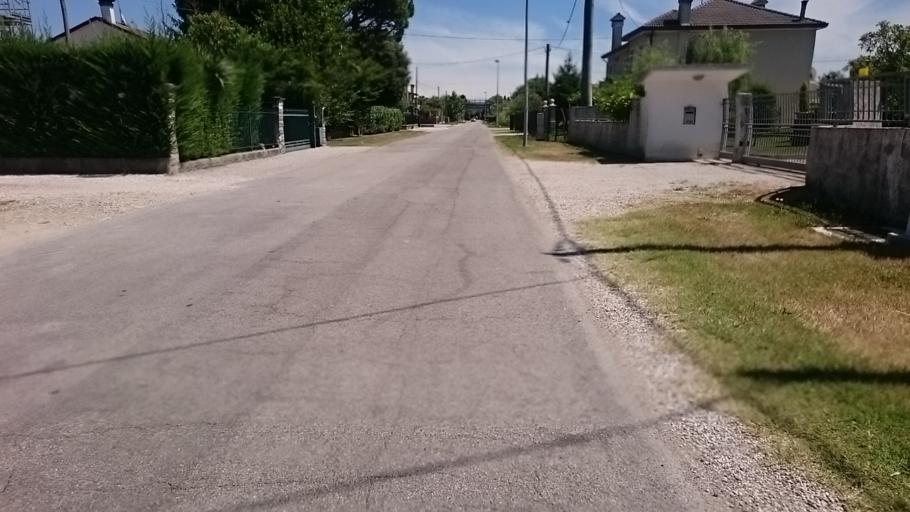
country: IT
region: Veneto
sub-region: Provincia di Padova
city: Borgoricco-San Michele delle Badesse-Sant'Eufemia
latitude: 45.5338
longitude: 11.9398
